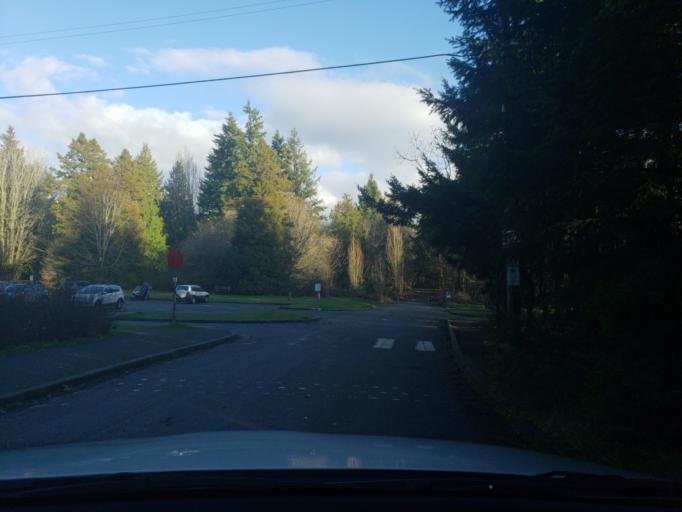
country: US
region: Washington
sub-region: King County
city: Seattle
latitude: 47.6544
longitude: -122.4107
